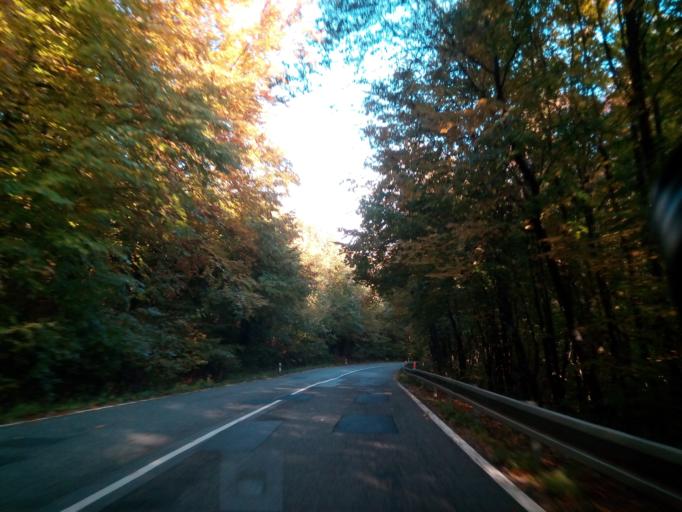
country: SK
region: Kosicky
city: Kosice
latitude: 48.7771
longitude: 21.1437
